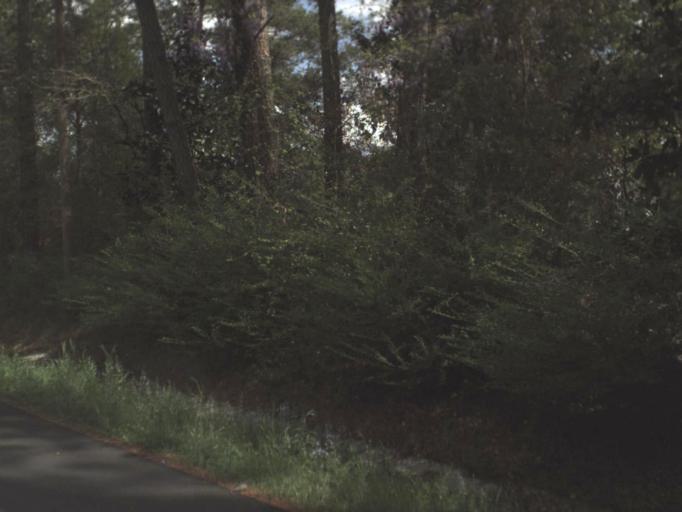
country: US
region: Alabama
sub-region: Covington County
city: Florala
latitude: 30.9666
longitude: -86.3905
